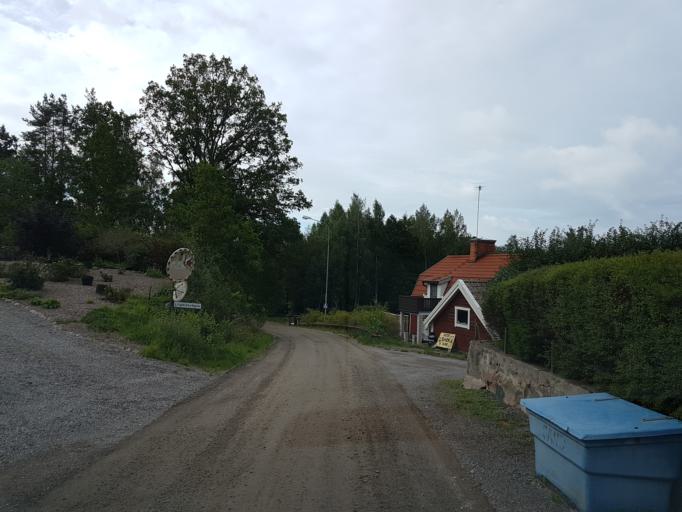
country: SE
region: OEstergoetland
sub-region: Atvidabergs Kommun
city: Atvidaberg
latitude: 58.2147
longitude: 16.0246
